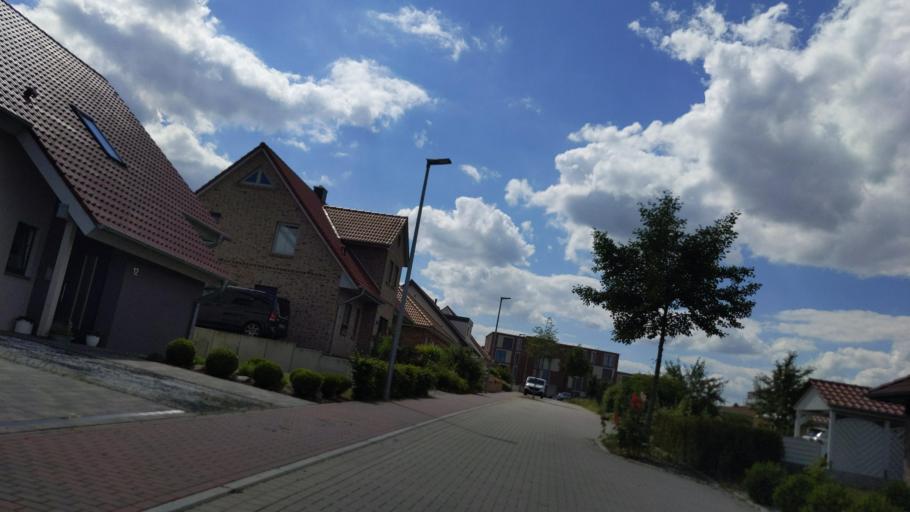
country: DE
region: Schleswig-Holstein
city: Neustadt in Holstein
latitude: 54.1089
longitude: 10.8346
